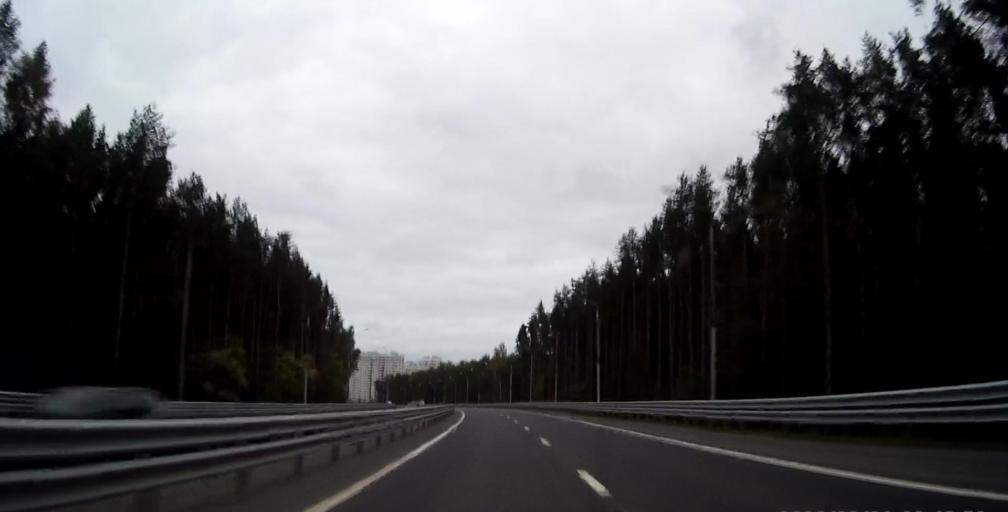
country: RU
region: Moskovskaya
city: Dubrovitsy
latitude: 55.4053
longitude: 37.5016
